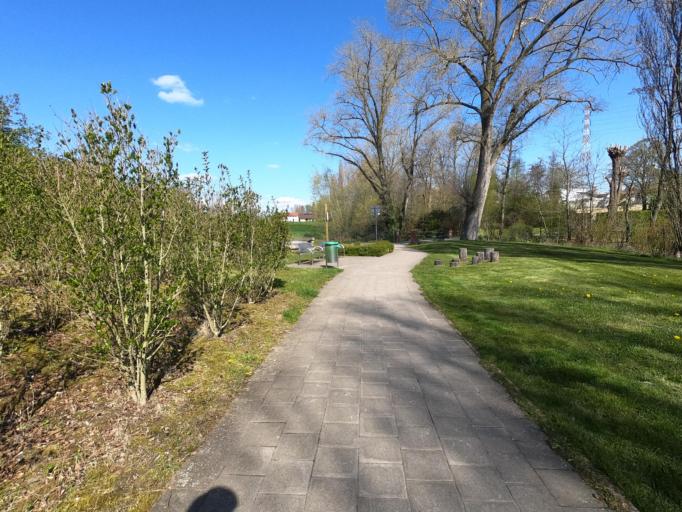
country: BE
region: Flanders
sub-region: Provincie West-Vlaanderen
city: Wevelgem
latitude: 50.7888
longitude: 3.1635
